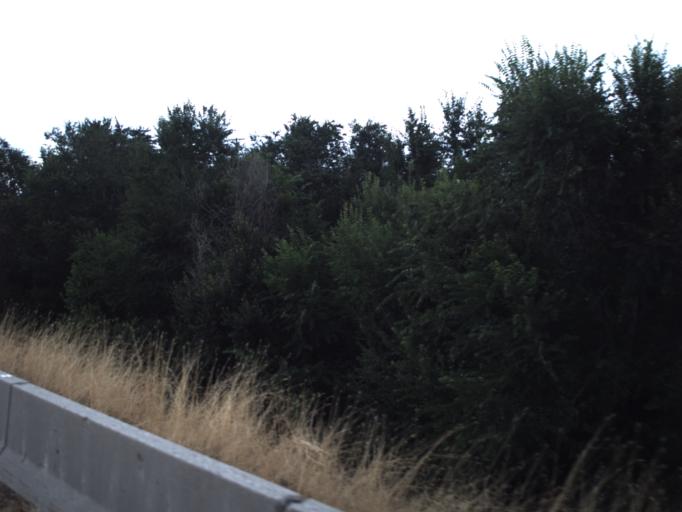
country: US
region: Utah
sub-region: Morgan County
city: Morgan
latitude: 40.9929
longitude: -111.6816
